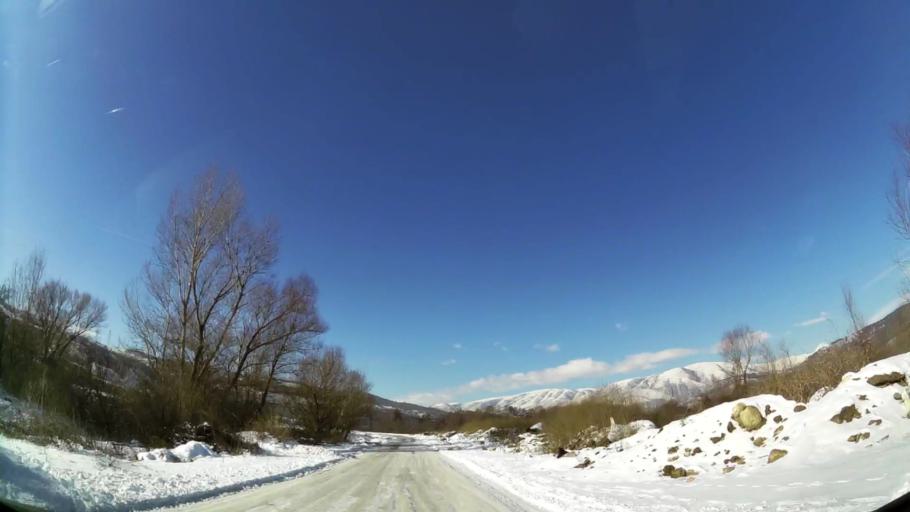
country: MK
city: Ljubin
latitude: 42.0050
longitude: 21.3051
